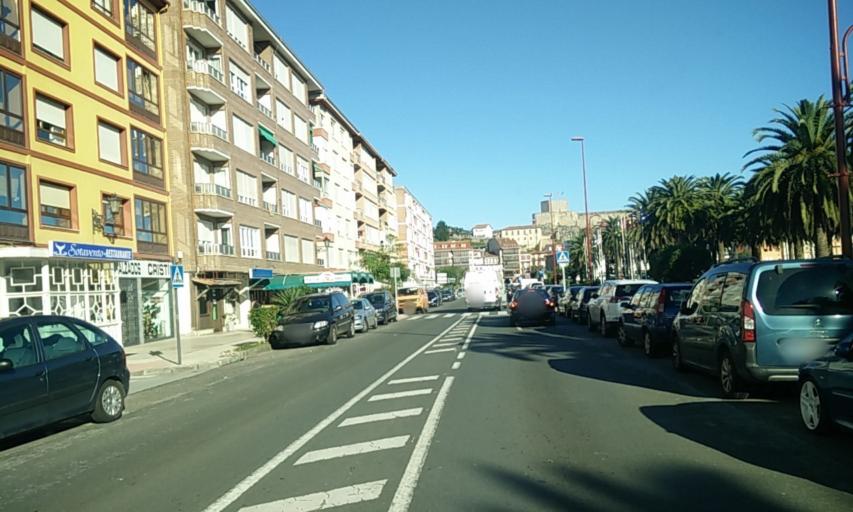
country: ES
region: Cantabria
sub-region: Provincia de Cantabria
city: San Vicente de la Barquera
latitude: 43.3825
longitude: -4.3980
